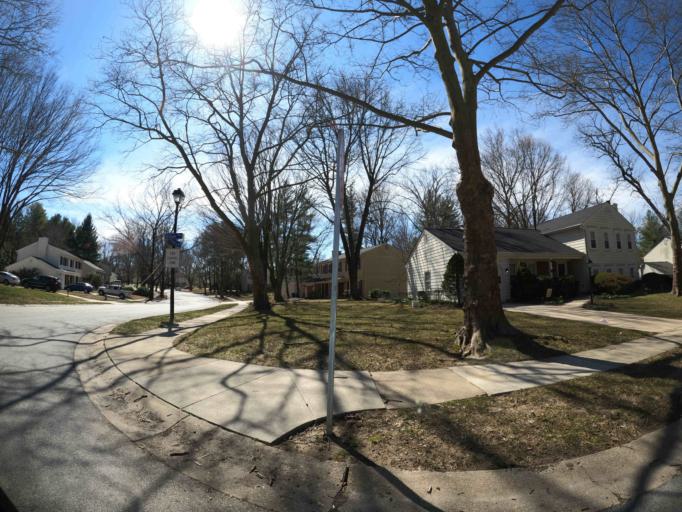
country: US
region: Maryland
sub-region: Howard County
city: Columbia
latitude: 39.2204
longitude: -76.8247
